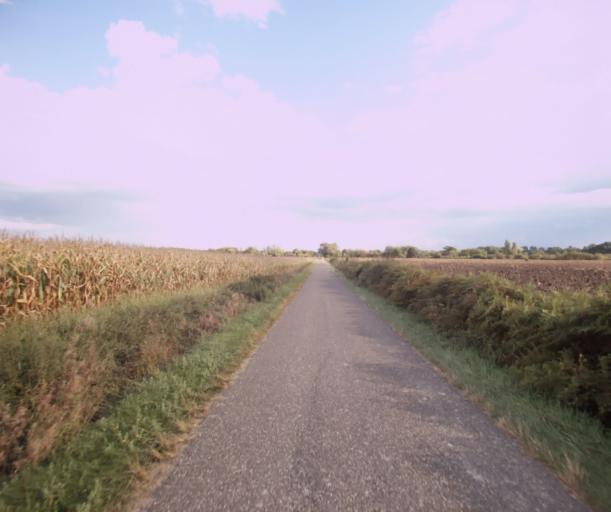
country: FR
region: Midi-Pyrenees
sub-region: Departement du Gers
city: Cazaubon
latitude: 43.9131
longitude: -0.0663
